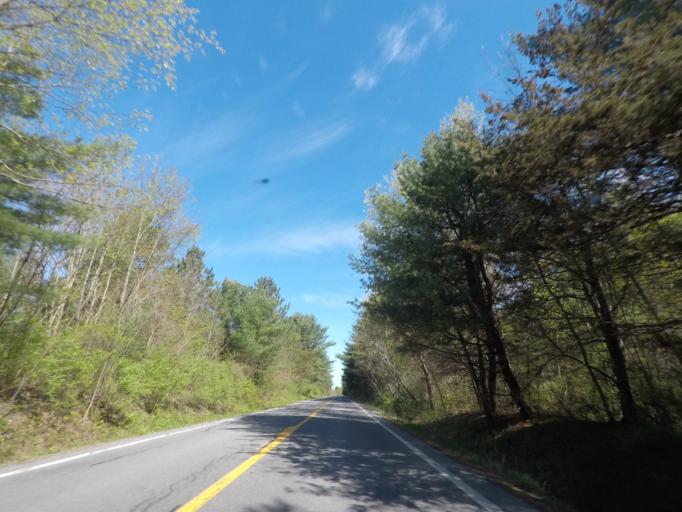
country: US
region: New York
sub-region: Albany County
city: Ravena
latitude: 42.4948
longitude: -73.9420
